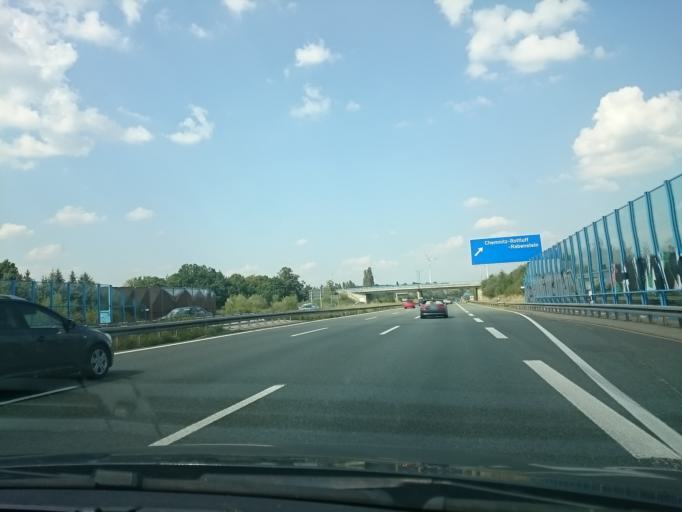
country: DE
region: Saxony
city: Neukirchen
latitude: 50.8266
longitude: 12.8510
